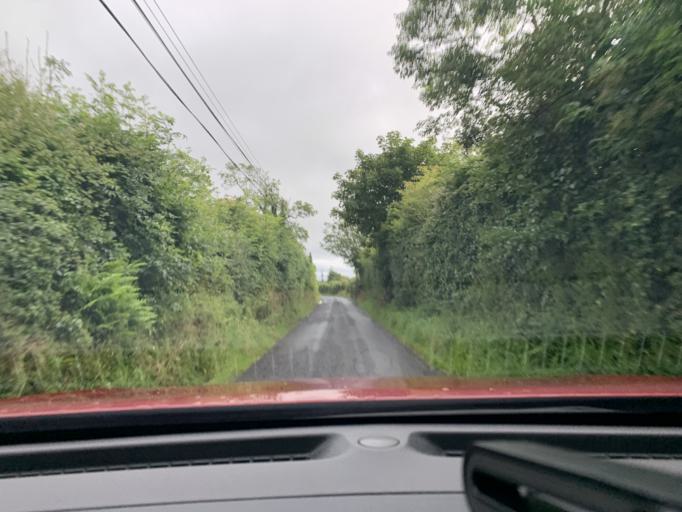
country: IE
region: Connaught
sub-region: Sligo
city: Strandhill
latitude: 54.3602
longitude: -8.5382
